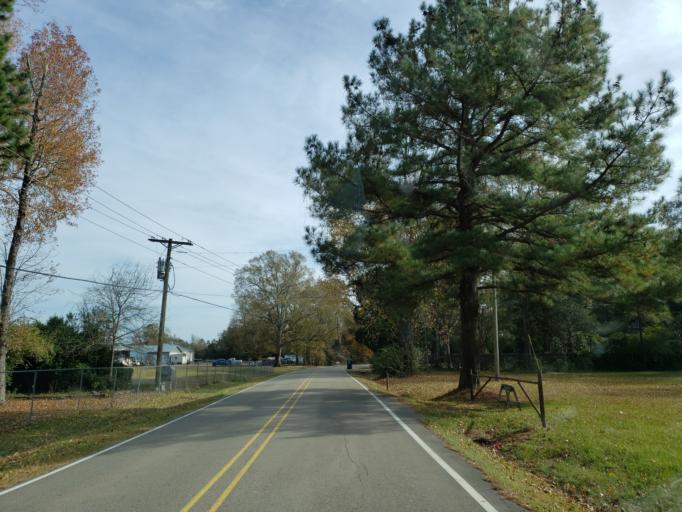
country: US
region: Mississippi
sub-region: Forrest County
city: Rawls Springs
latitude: 31.3846
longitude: -89.3731
